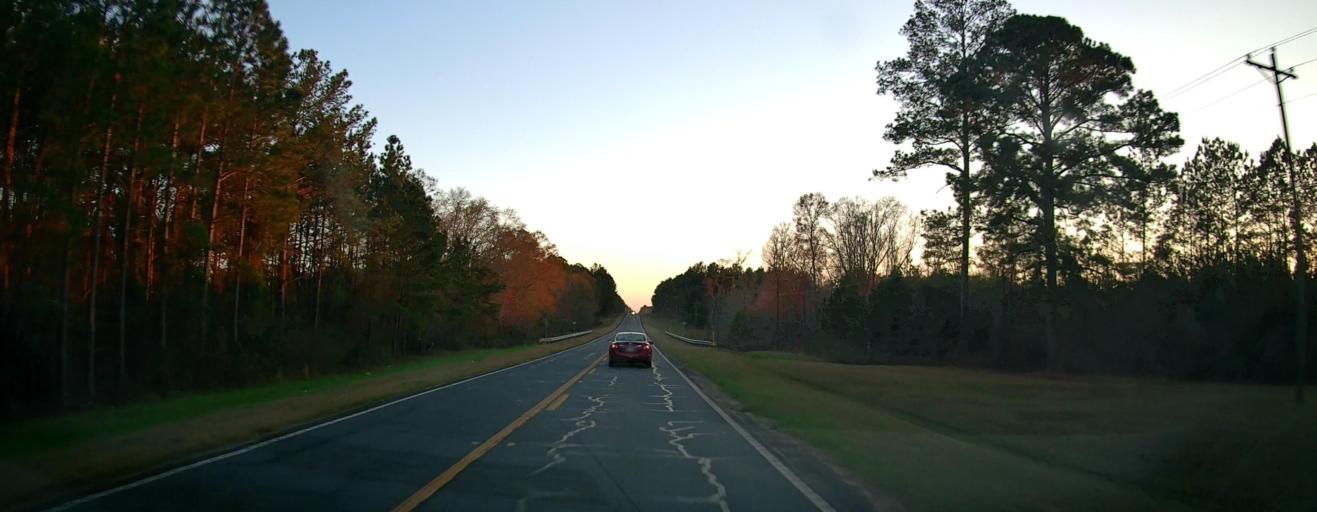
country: US
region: Georgia
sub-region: Dodge County
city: Eastman
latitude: 32.2385
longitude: -83.1480
